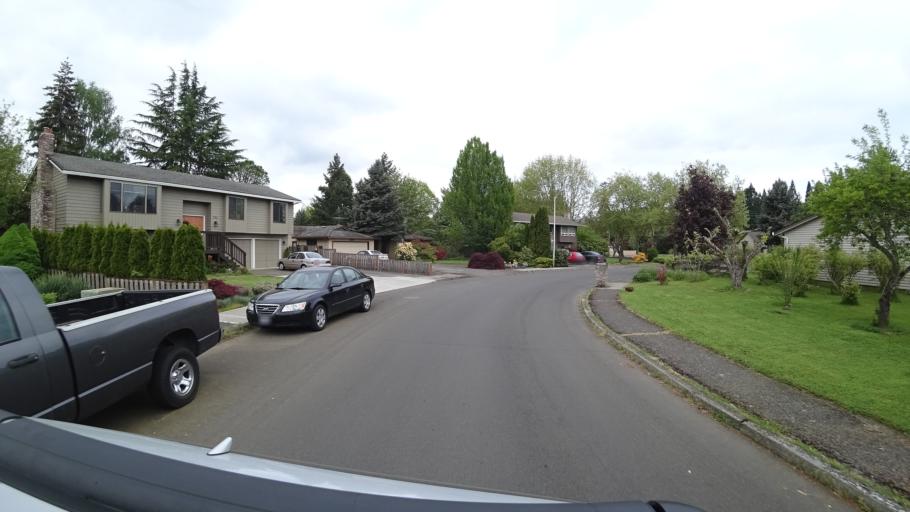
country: US
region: Oregon
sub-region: Washington County
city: Hillsboro
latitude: 45.5335
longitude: -122.9785
